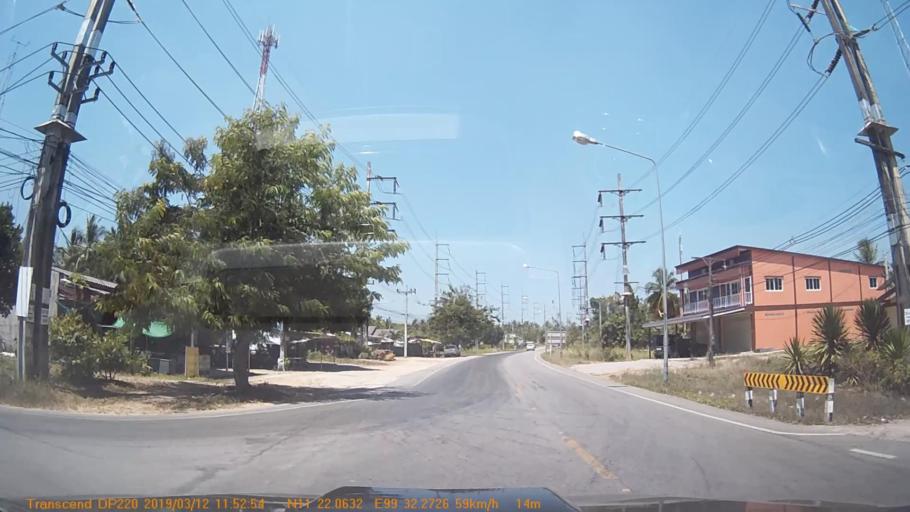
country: TH
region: Prachuap Khiri Khan
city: Thap Sakae
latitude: 11.3677
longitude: 99.5378
